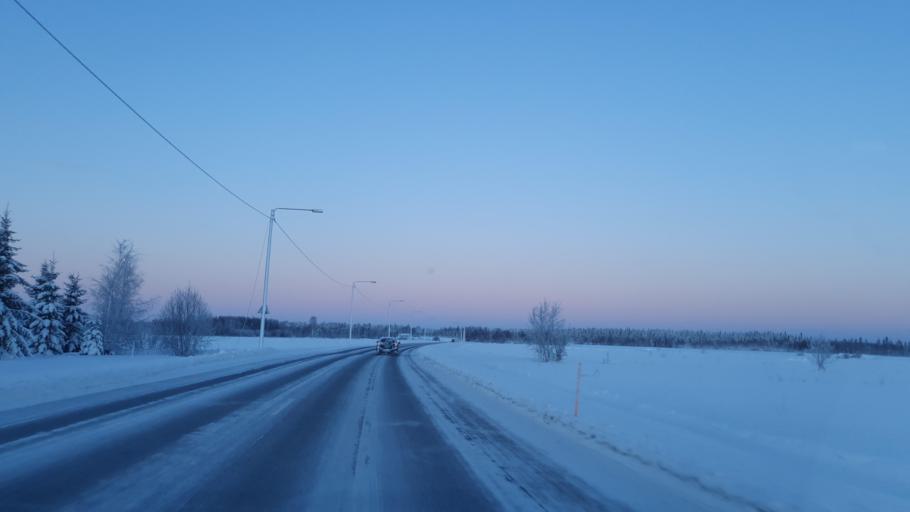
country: FI
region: Lapland
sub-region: Kemi-Tornio
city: Tornio
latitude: 65.9871
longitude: 24.0691
